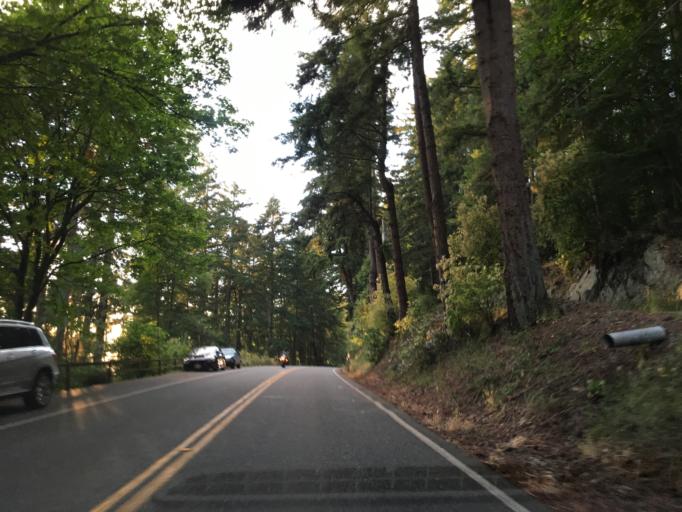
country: US
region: Washington
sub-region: Whatcom County
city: Geneva
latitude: 48.6108
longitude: -122.4350
